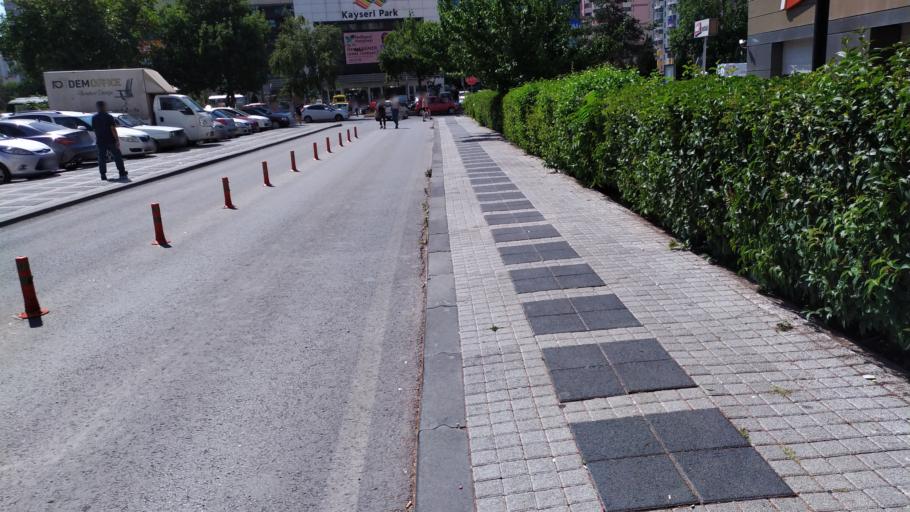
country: TR
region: Kayseri
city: Kayseri
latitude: 38.7277
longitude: 35.5198
